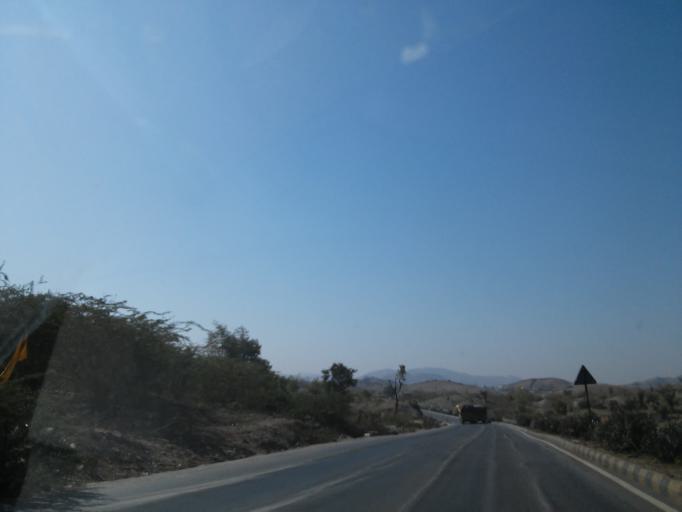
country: IN
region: Rajasthan
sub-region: Dungarpur
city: Dungarpur
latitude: 24.0636
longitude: 73.6755
